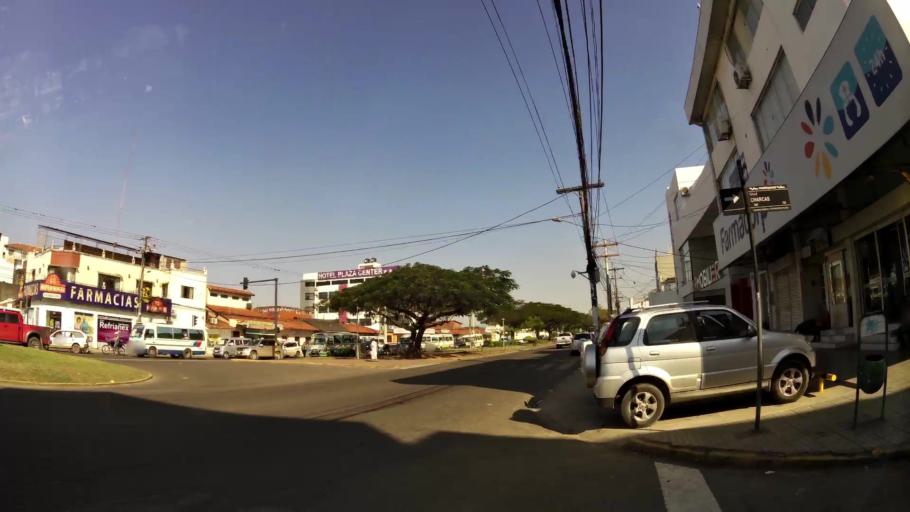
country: BO
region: Santa Cruz
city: Santa Cruz de la Sierra
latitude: -17.7796
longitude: -63.1729
